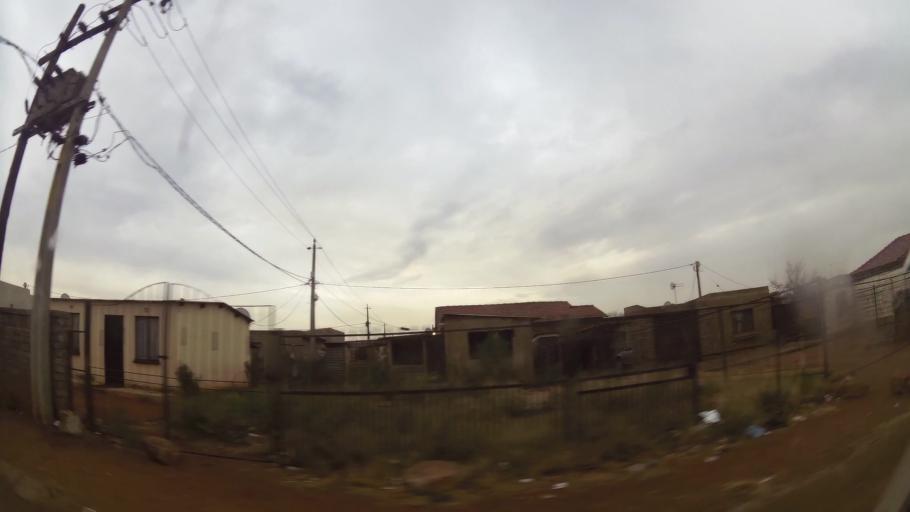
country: ZA
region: Gauteng
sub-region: Ekurhuleni Metropolitan Municipality
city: Germiston
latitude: -26.3810
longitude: 28.1772
